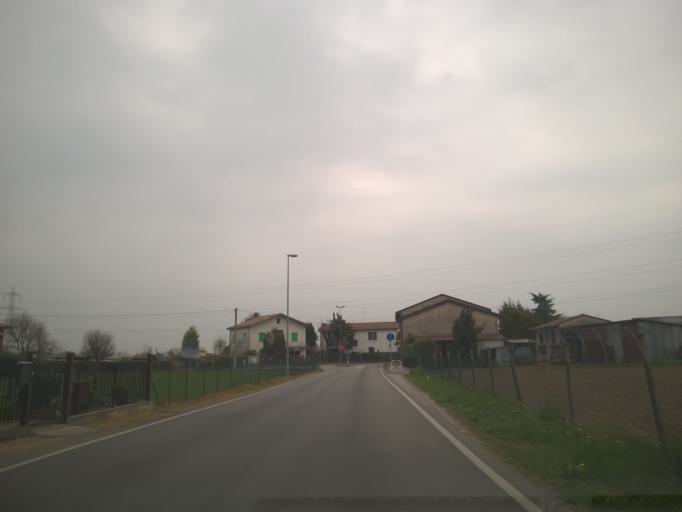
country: IT
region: Veneto
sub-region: Provincia di Vicenza
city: Sandrigo
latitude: 45.6509
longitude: 11.6040
